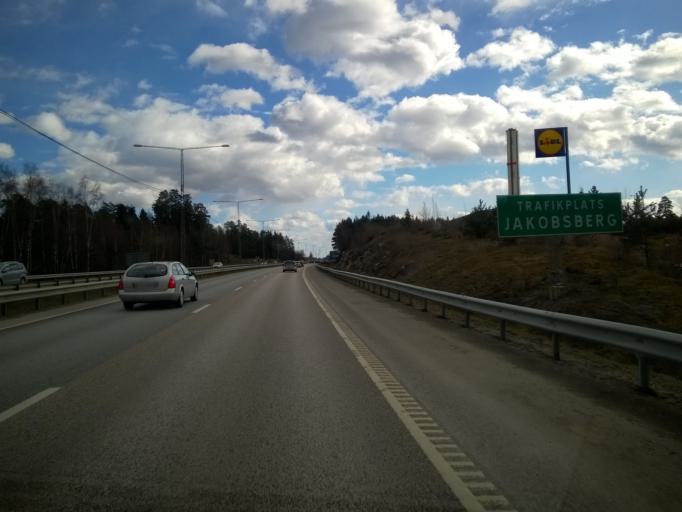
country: SE
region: Stockholm
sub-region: Jarfalla Kommun
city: Jakobsberg
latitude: 59.4293
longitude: 17.8488
